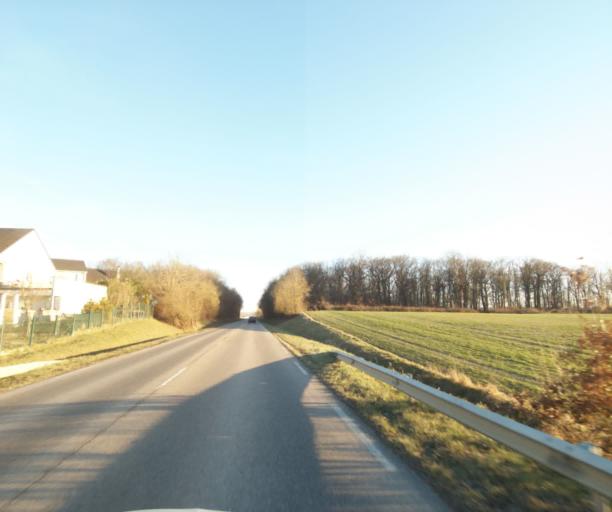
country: FR
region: Lorraine
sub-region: Departement de Meurthe-et-Moselle
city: Laneuveville-devant-Nancy
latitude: 48.6730
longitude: 6.2295
